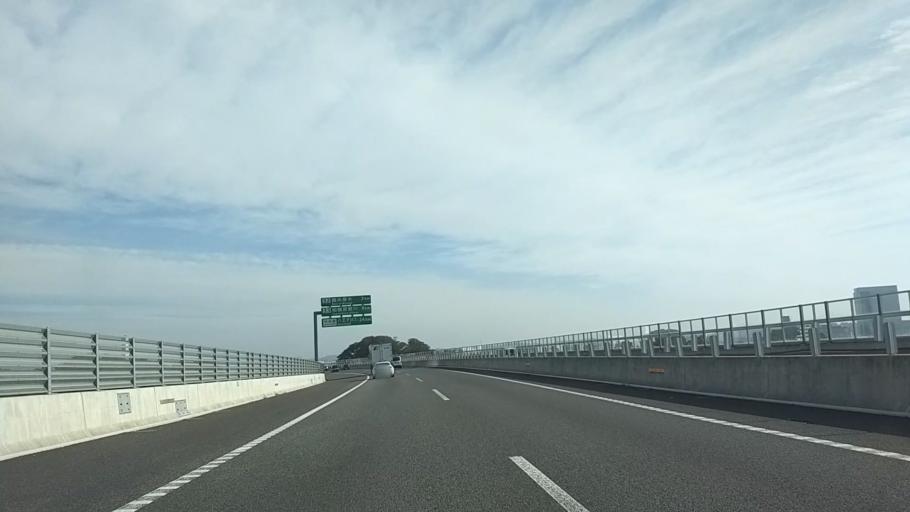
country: JP
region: Kanagawa
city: Atsugi
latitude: 35.4499
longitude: 139.3740
